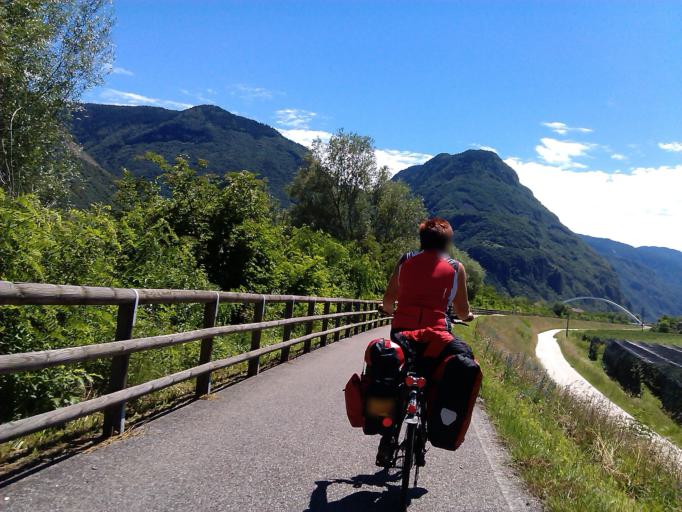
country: IT
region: Trentino-Alto Adige
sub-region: Bolzano
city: Vadena
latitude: 46.4184
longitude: 11.3142
